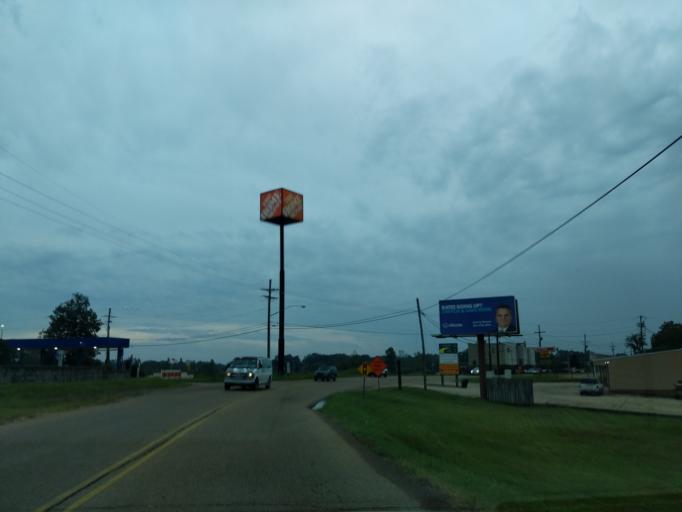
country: US
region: Mississippi
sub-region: Warren County
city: Vicksburg
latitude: 32.3187
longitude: -90.8748
